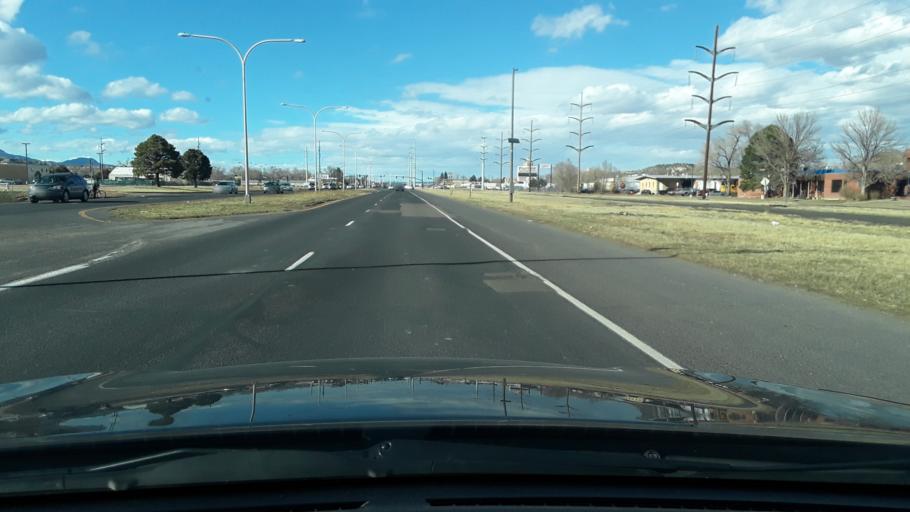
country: US
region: Colorado
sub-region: El Paso County
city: Colorado Springs
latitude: 38.8825
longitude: -104.8187
